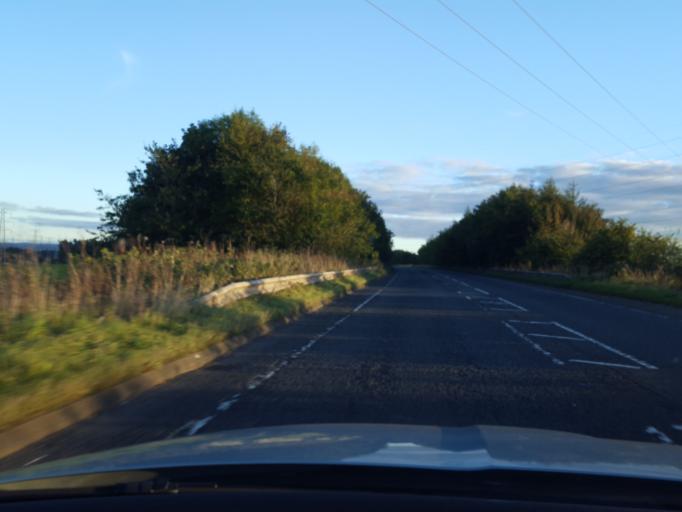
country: GB
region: Scotland
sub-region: West Lothian
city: Armadale
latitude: 55.8928
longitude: -3.6766
